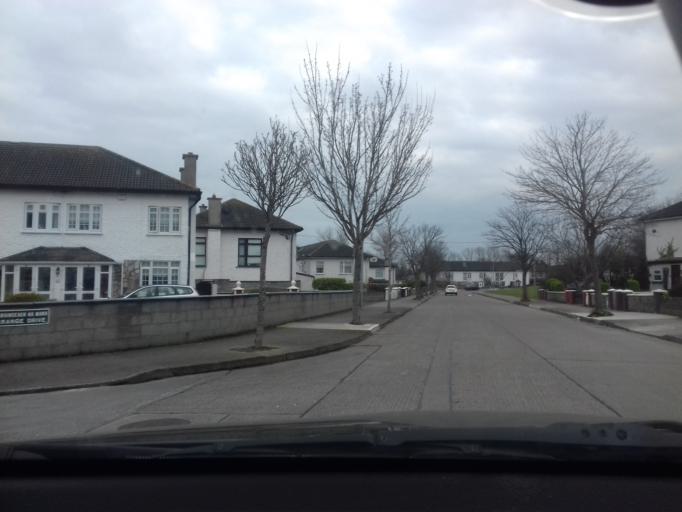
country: IE
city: Bayside
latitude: 53.3950
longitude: -6.1388
